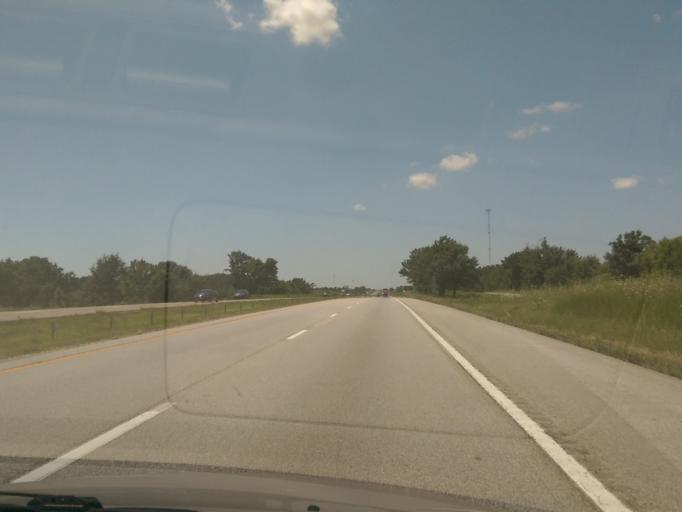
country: US
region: Missouri
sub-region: Cooper County
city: Boonville
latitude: 38.9353
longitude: -92.8175
